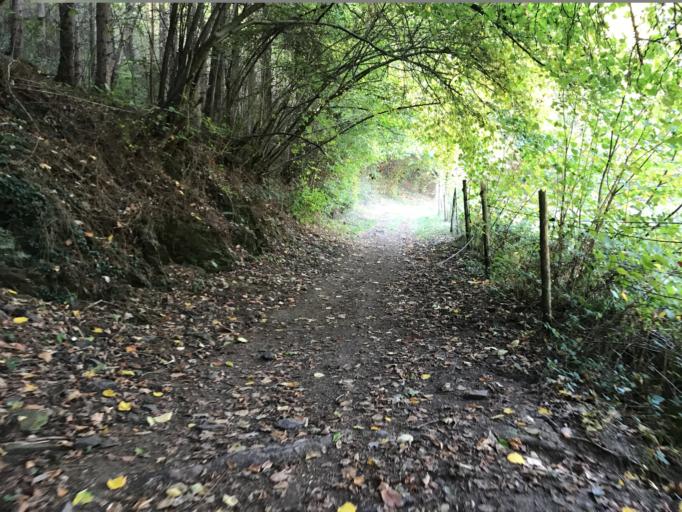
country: DE
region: Rheinland-Pfalz
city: Kobern-Gondorf
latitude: 50.2948
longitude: 7.4449
